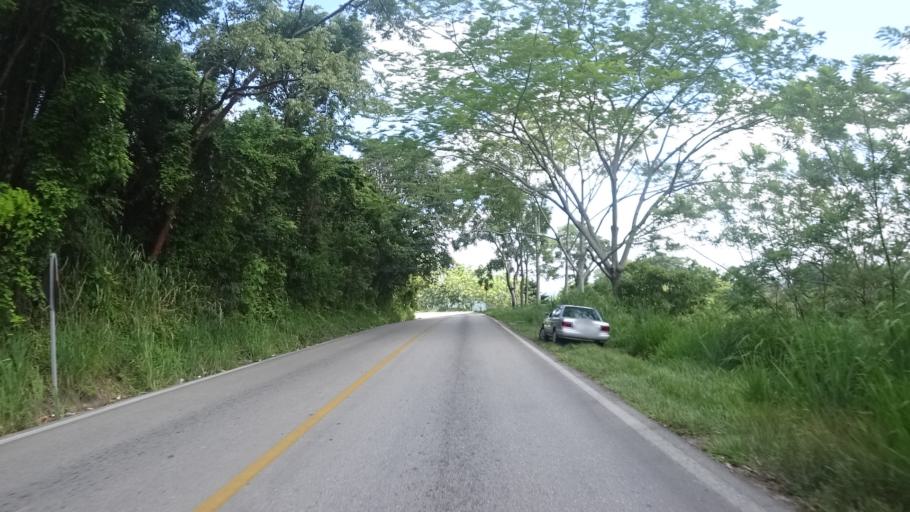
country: MX
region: Chiapas
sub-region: Palenque
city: Doctor Samuel Leon Brindis
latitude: 17.4670
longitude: -91.9634
